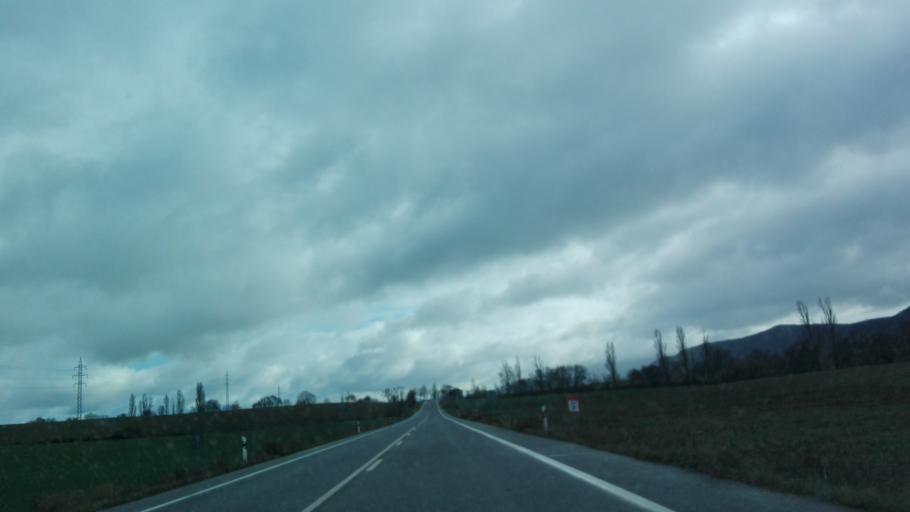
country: ES
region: Navarre
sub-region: Provincia de Navarra
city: Lizoain
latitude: 42.8160
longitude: -1.5093
